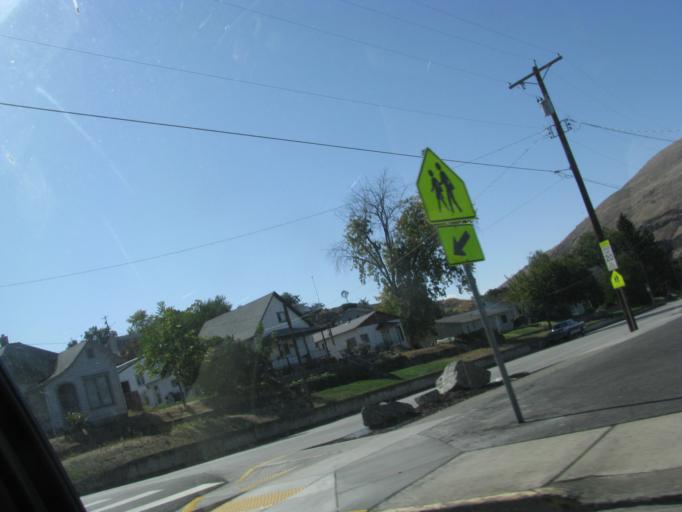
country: US
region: Washington
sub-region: Asotin County
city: Asotin
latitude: 46.3399
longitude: -117.0487
